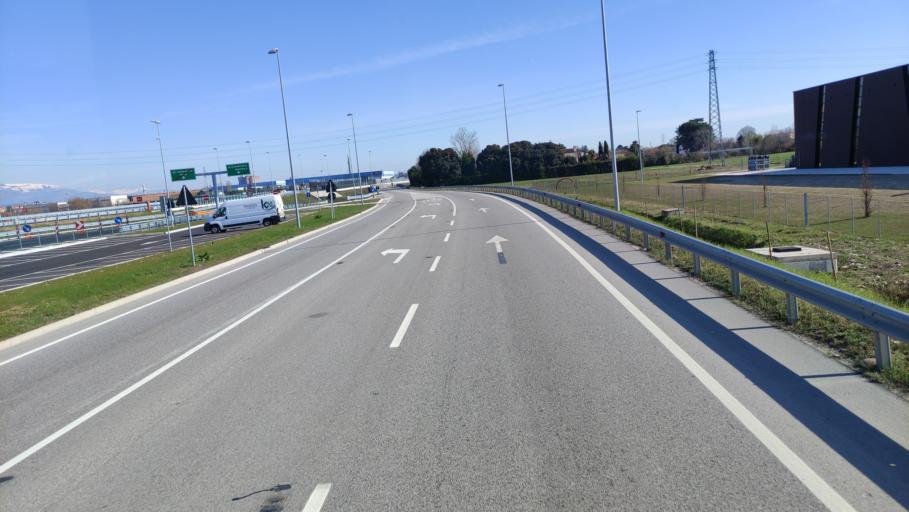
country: IT
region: Veneto
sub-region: Provincia di Vicenza
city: Bassano del Grappa
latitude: 45.7374
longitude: 11.7171
